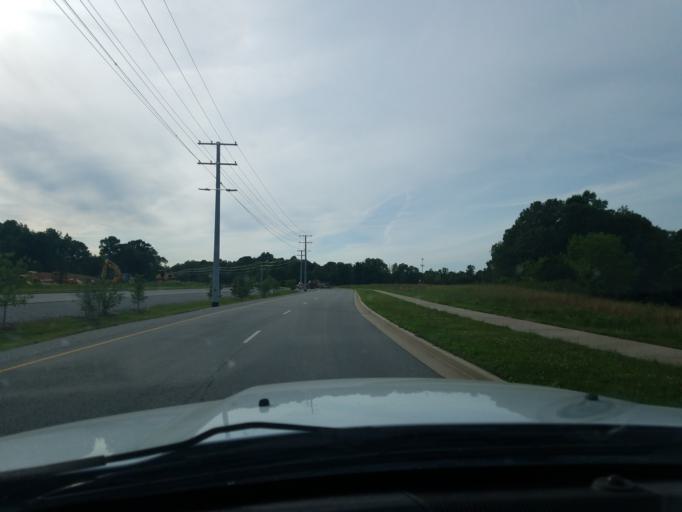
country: US
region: Tennessee
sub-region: Putnam County
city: Cookeville
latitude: 36.1301
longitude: -85.5511
